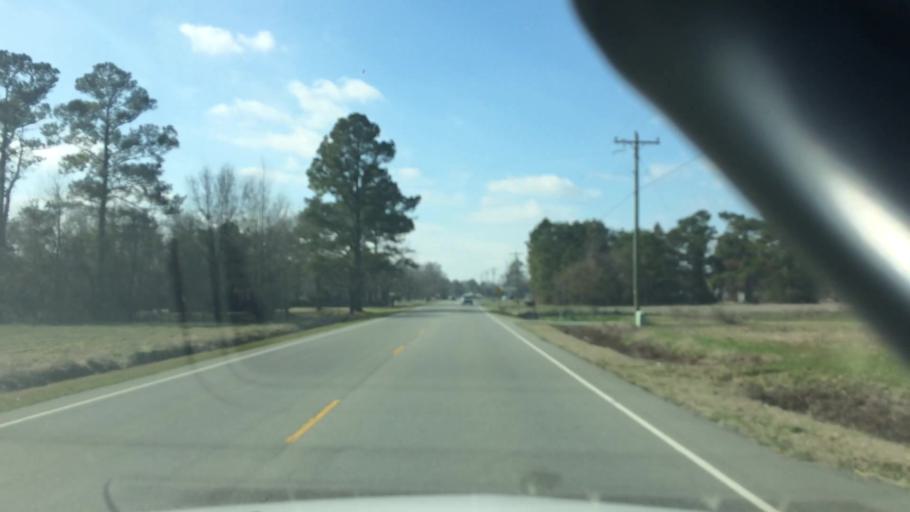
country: US
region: North Carolina
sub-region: Duplin County
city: Wallace
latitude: 34.7860
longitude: -77.8995
